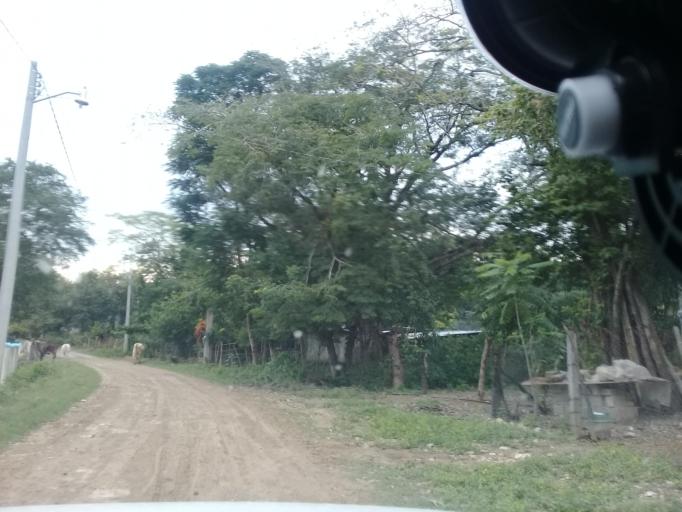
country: MX
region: Hidalgo
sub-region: Huejutla de Reyes
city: Chalahuiyapa
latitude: 21.1644
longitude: -98.3484
